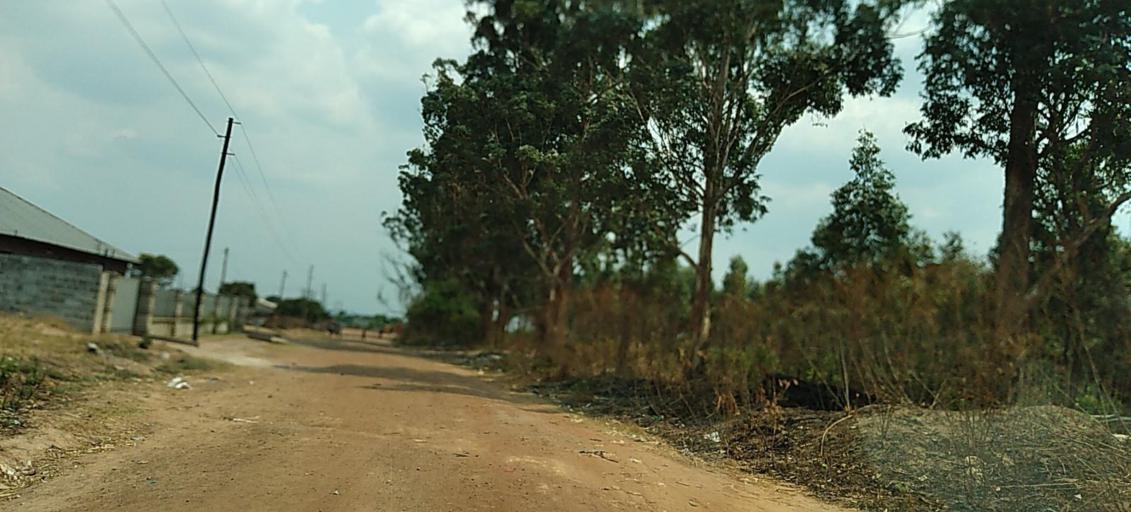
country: ZM
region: Copperbelt
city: Kalulushi
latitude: -12.8498
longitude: 28.0781
